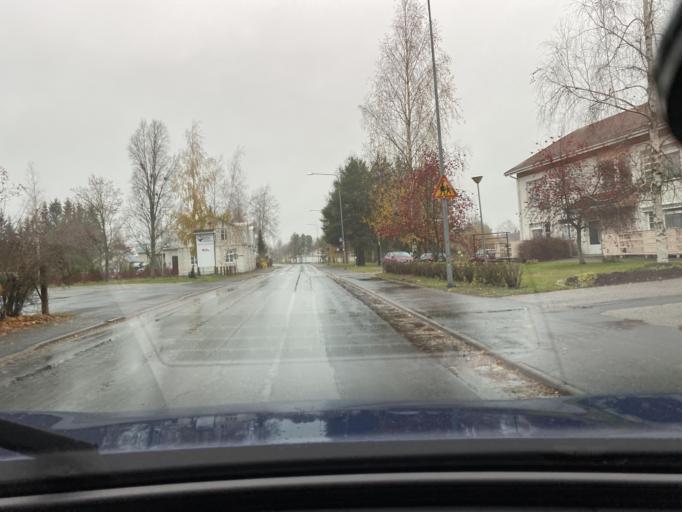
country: FI
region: Varsinais-Suomi
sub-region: Loimaa
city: Loimaa
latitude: 60.8551
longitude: 23.0520
